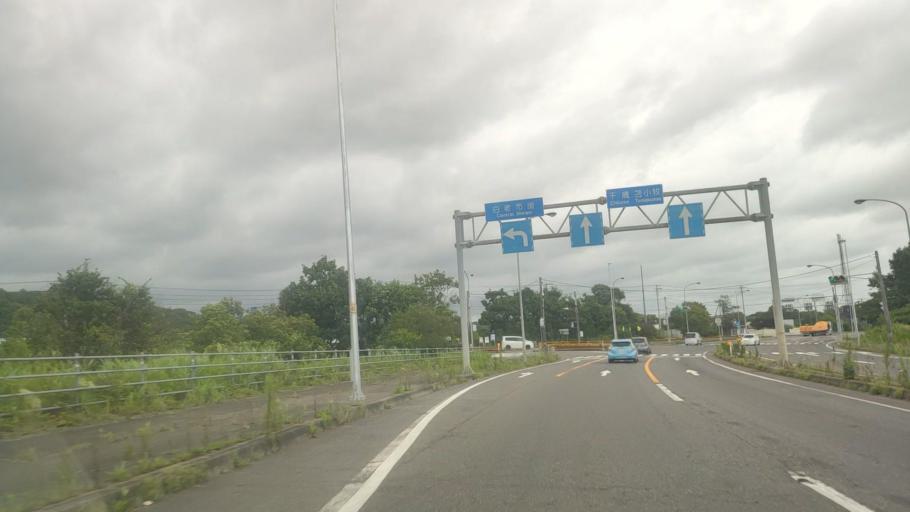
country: JP
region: Hokkaido
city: Shiraoi
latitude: 42.5632
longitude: 141.3814
